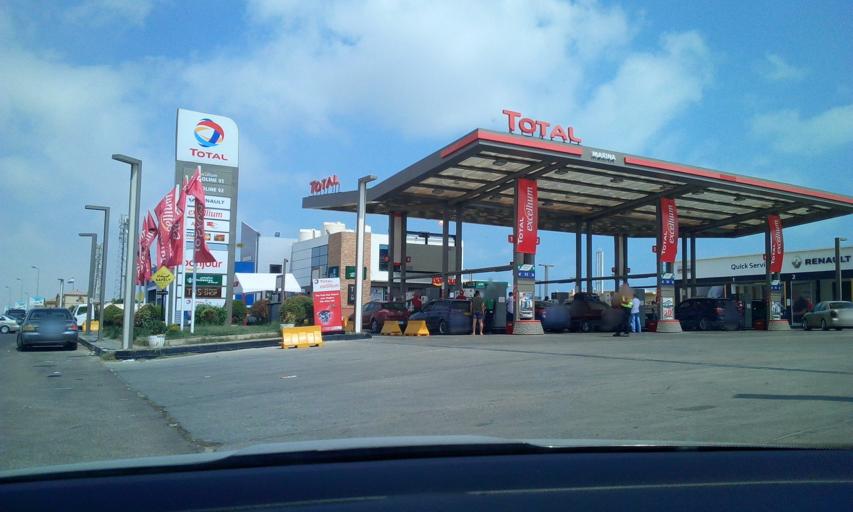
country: EG
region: Muhafazat Matruh
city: Al `Alamayn
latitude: 30.8353
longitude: 28.9610
